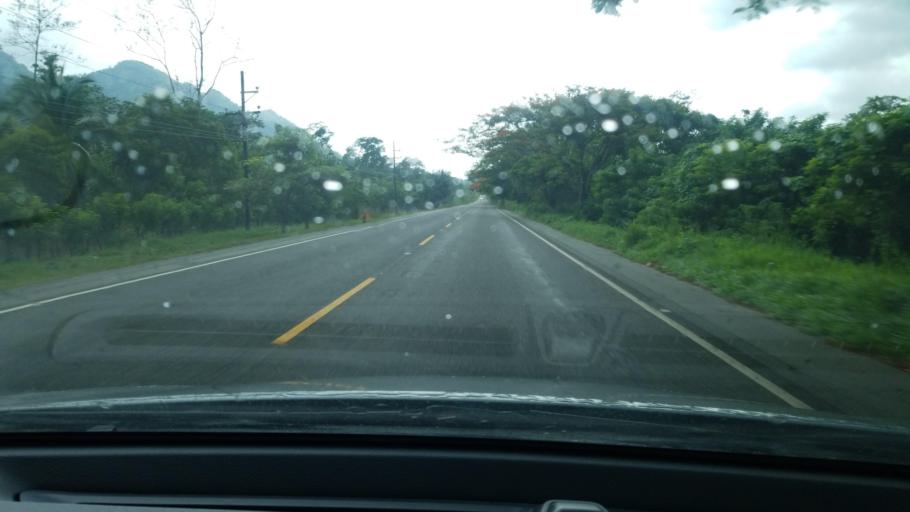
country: HN
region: Cortes
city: Rio Chiquito
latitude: 15.6221
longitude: -88.2649
